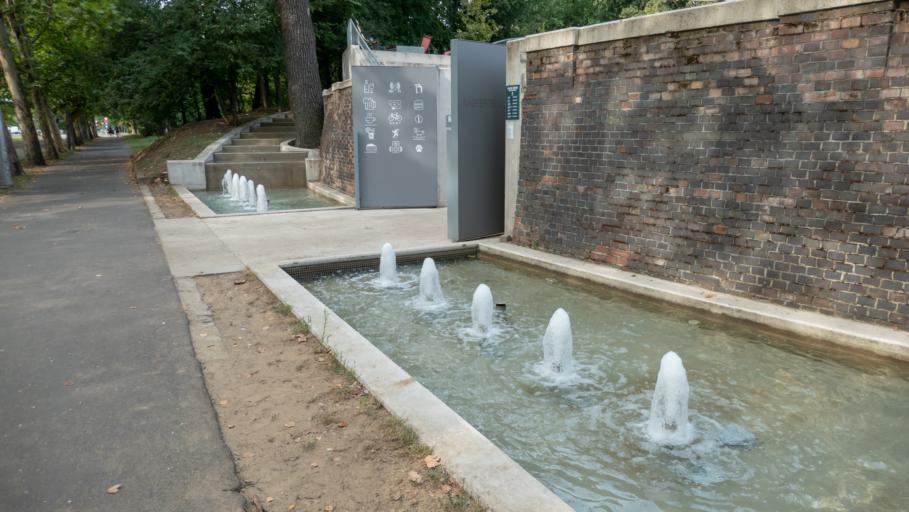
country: HU
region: Hajdu-Bihar
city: Debrecen
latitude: 47.5546
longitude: 21.6306
